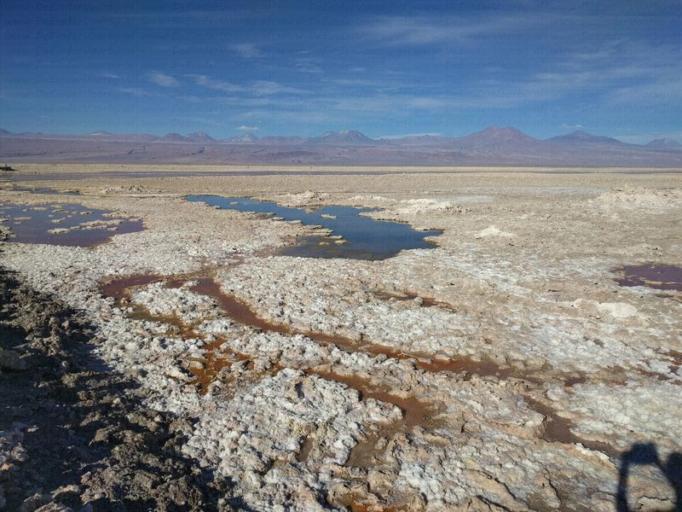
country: CL
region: Antofagasta
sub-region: Provincia de El Loa
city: San Pedro de Atacama
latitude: -23.2894
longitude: -68.1783
